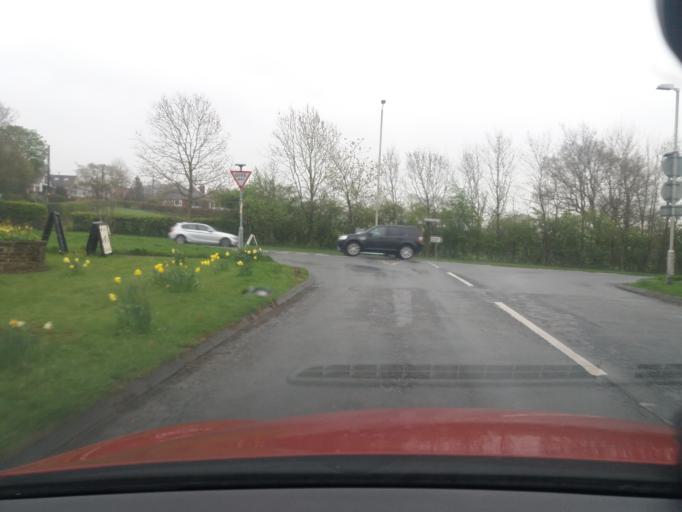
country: GB
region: England
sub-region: Lancashire
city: Chorley
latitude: 53.6824
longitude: -2.6094
